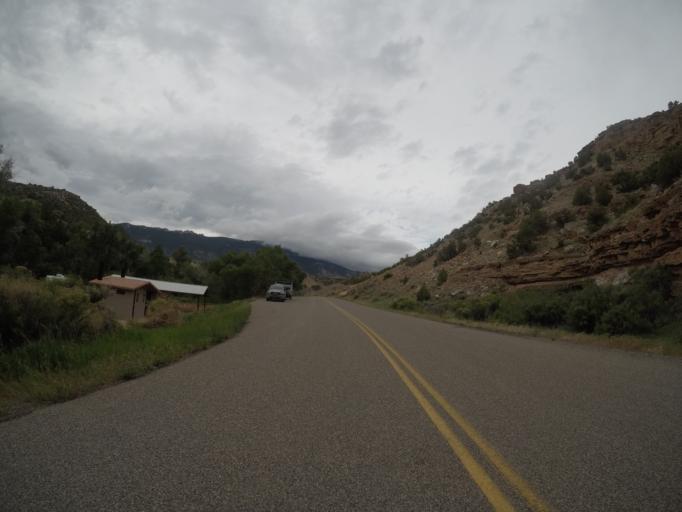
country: US
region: Wyoming
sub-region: Big Horn County
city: Lovell
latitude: 45.1066
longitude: -108.2265
